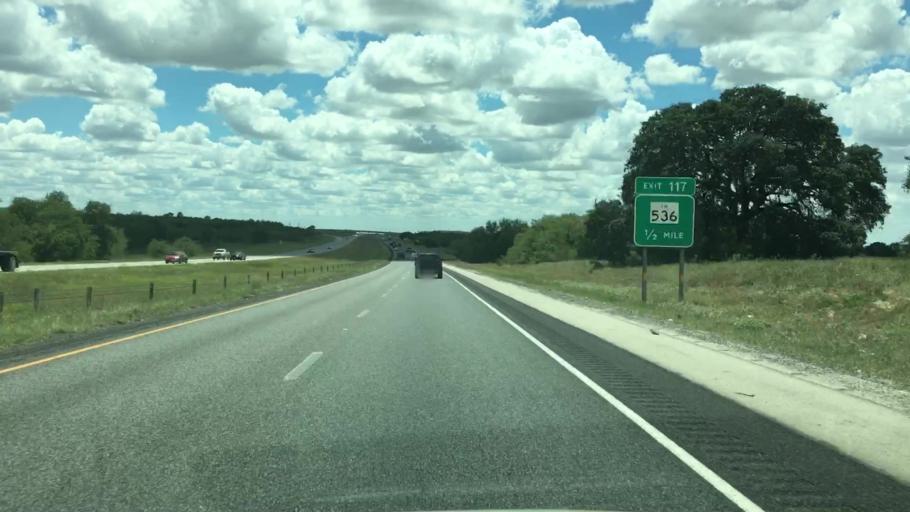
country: US
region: Texas
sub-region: Atascosa County
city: Poteet
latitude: 29.1173
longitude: -98.4319
